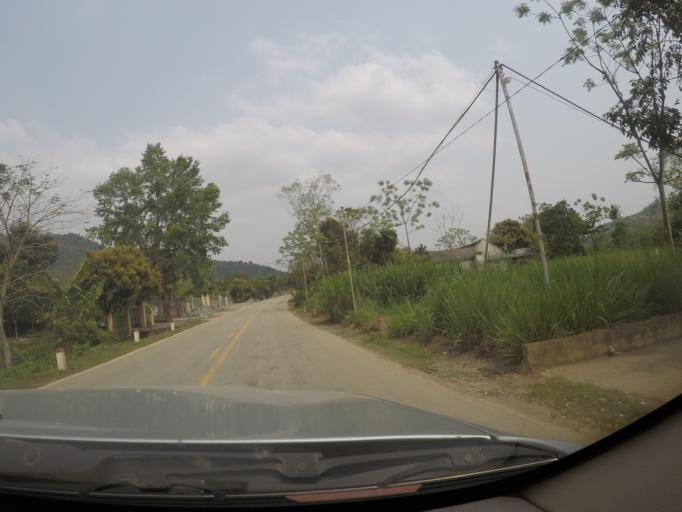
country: VN
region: Thanh Hoa
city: Thi Tran Yen Cat
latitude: 19.4783
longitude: 105.4092
